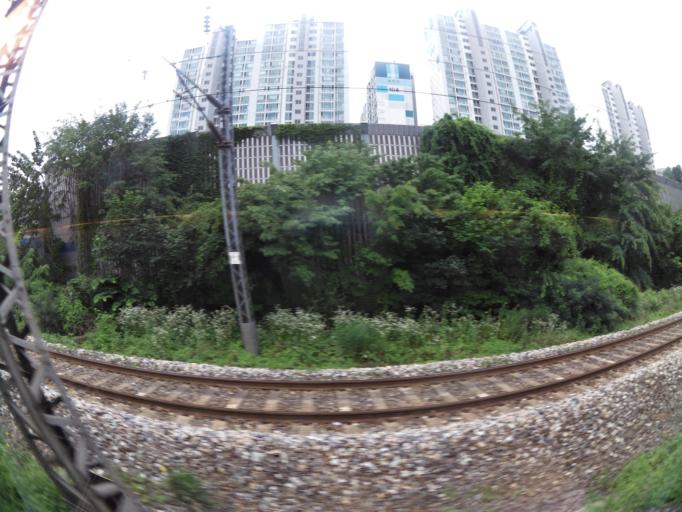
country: KR
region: Gyeonggi-do
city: Suwon-si
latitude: 37.2980
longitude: 126.9781
